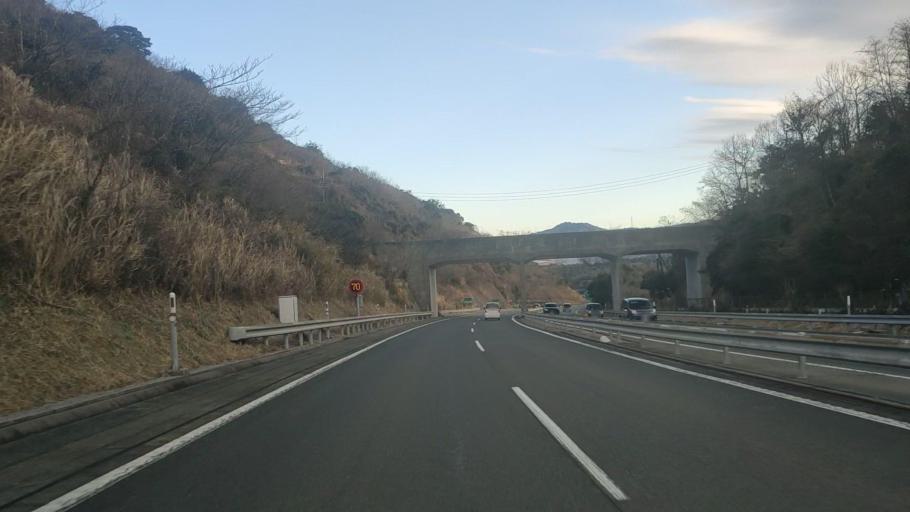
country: JP
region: Oita
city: Hiji
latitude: 33.3638
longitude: 131.4519
